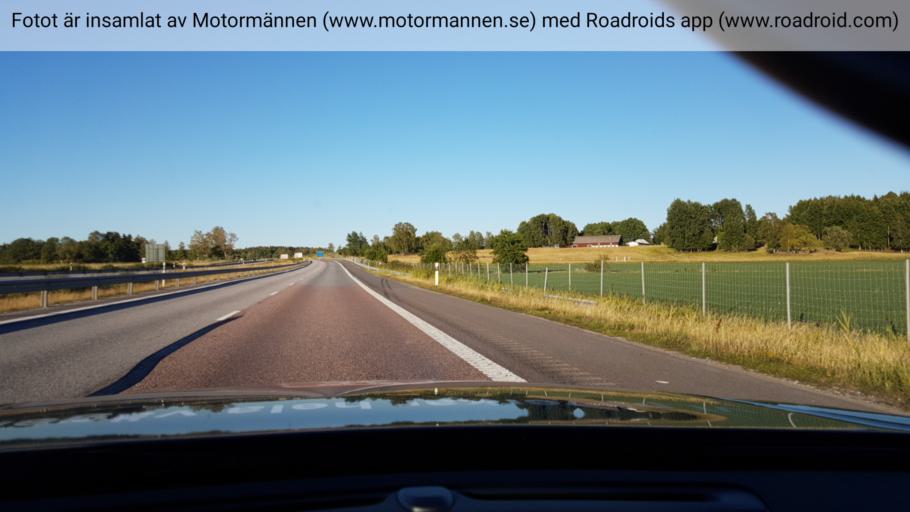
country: SE
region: OErebro
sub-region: Lindesbergs Kommun
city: Fellingsbro
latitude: 59.3295
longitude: 15.5141
